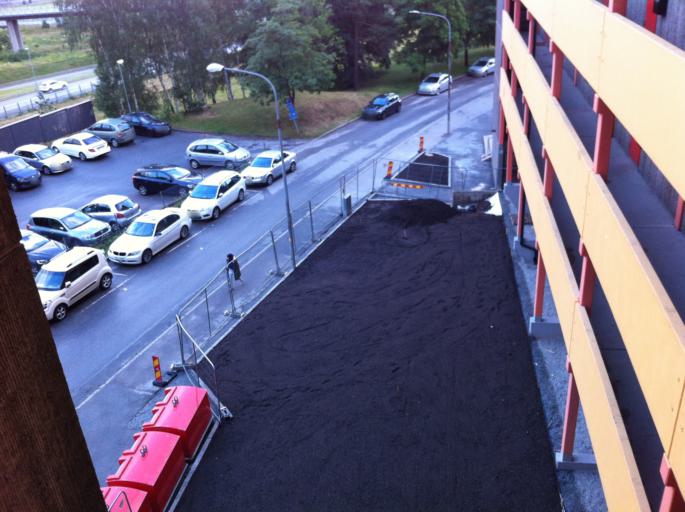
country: SE
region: Stockholm
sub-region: Stockholms Kommun
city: Kista
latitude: 59.3881
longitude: 17.9312
